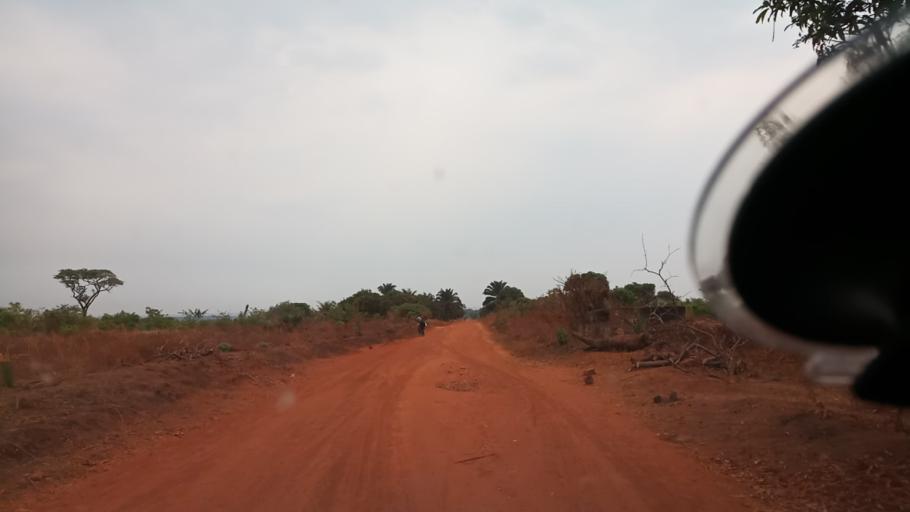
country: ZM
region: Luapula
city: Nchelenge
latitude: -9.1409
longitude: 28.2940
